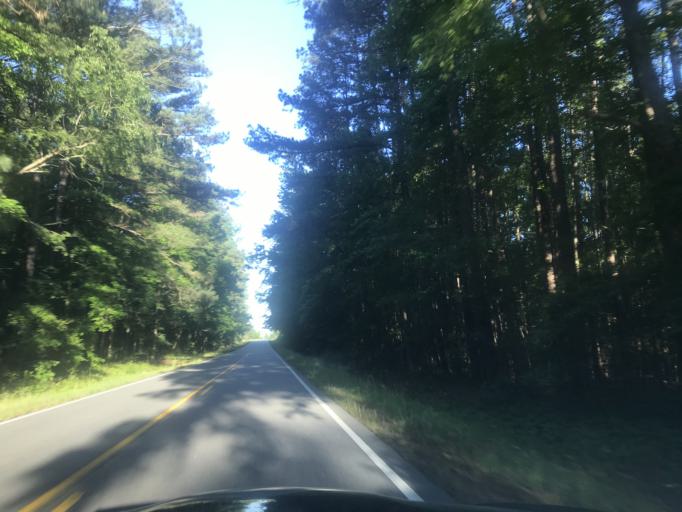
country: US
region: North Carolina
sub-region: Johnston County
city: Archer Lodge
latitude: 35.7303
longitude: -78.3947
